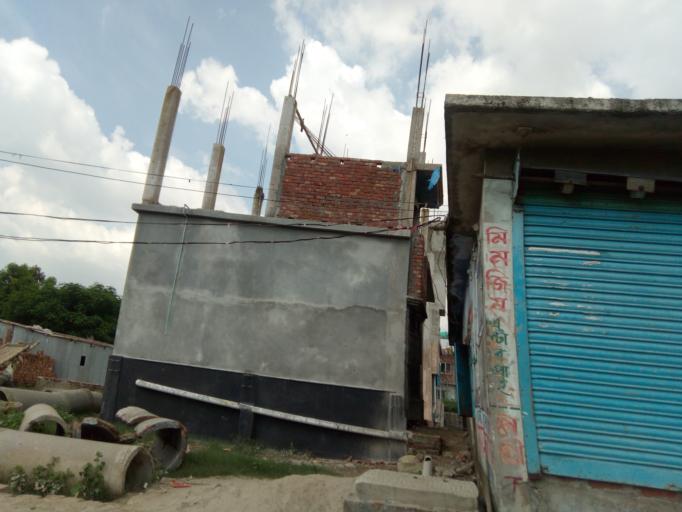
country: BD
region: Dhaka
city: Azimpur
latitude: 23.7285
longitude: 90.3606
